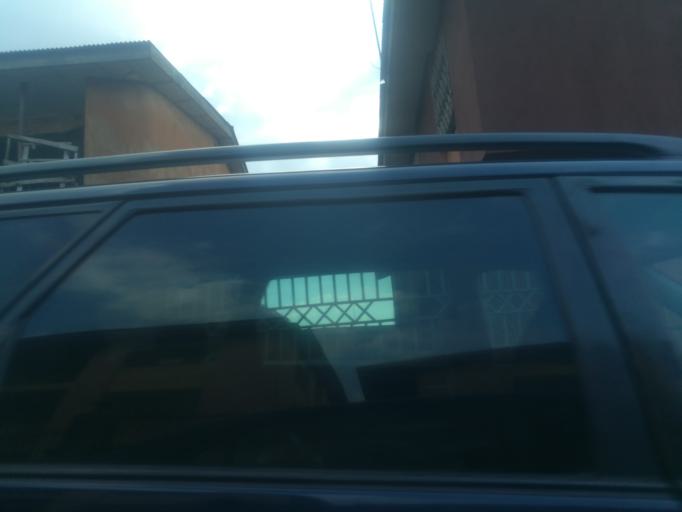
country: NG
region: Oyo
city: Ibadan
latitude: 7.4058
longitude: 3.9466
